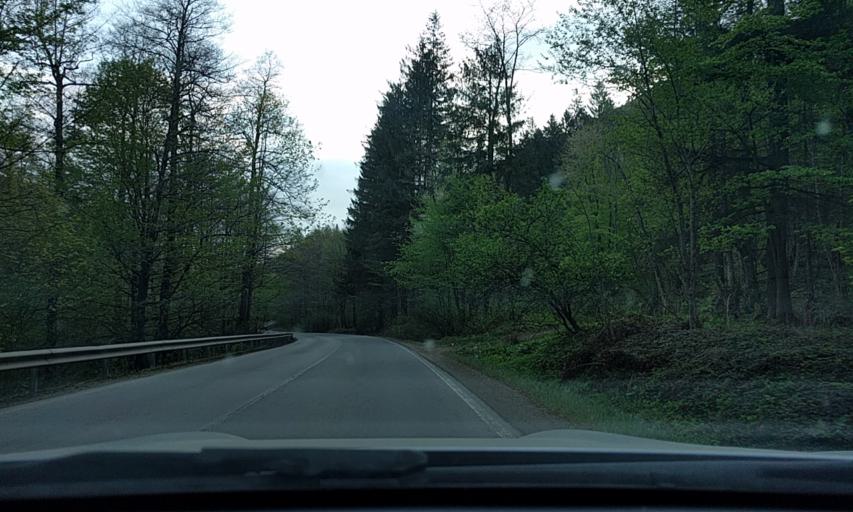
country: RO
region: Bacau
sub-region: Oras Slanic-Moldova
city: Slanic-Moldova
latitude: 46.1105
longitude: 26.4158
